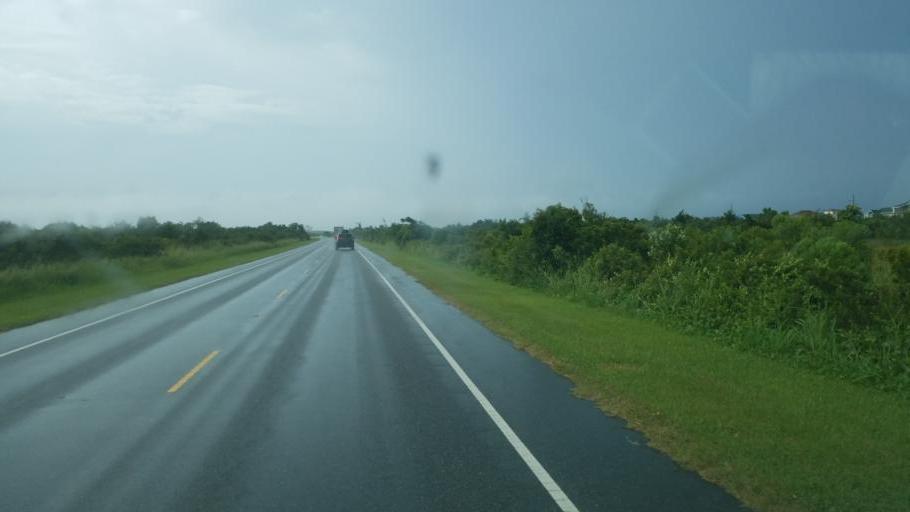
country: US
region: North Carolina
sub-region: Dare County
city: Wanchese
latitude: 35.8721
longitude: -75.5811
